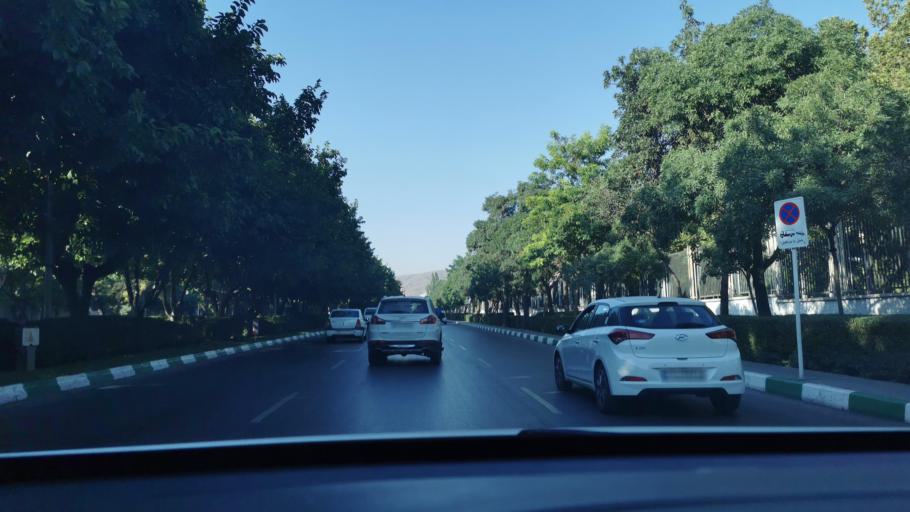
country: IR
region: Razavi Khorasan
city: Mashhad
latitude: 36.2973
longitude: 59.5617
